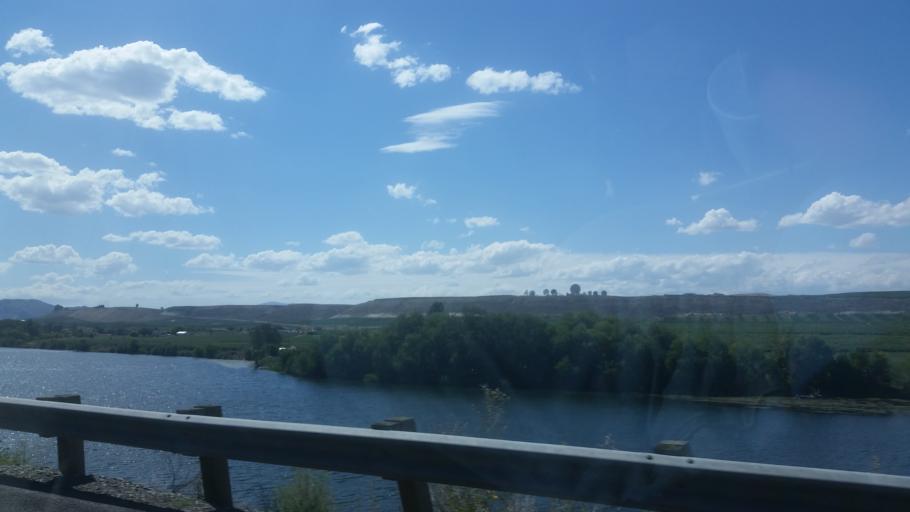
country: US
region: Washington
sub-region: Okanogan County
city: Brewster
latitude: 48.1502
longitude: -119.6648
